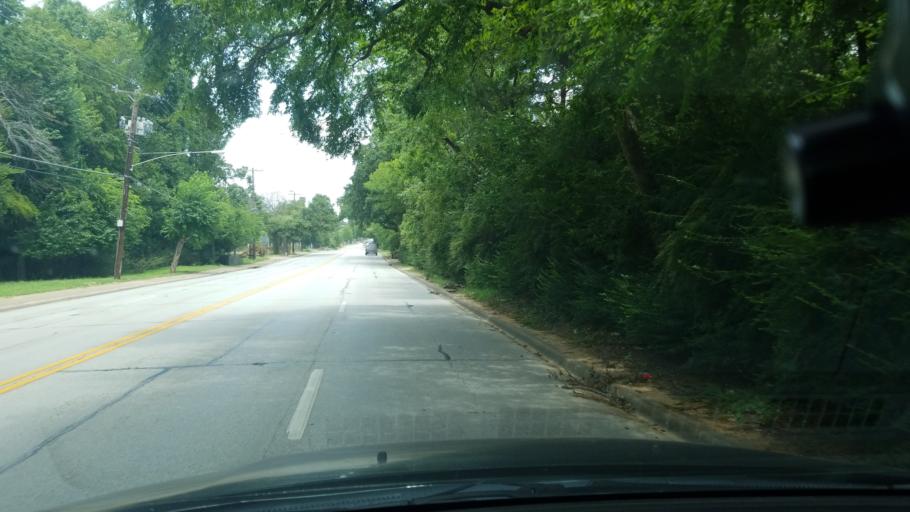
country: US
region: Texas
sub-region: Dallas County
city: Balch Springs
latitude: 32.7145
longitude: -96.6571
